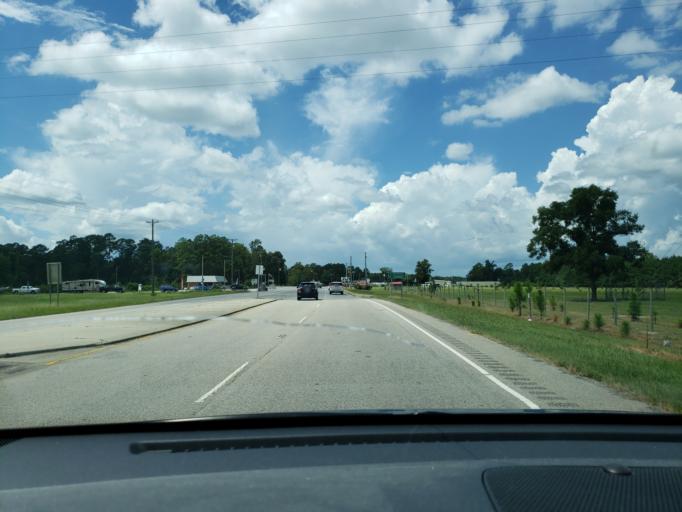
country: US
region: North Carolina
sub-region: Bladen County
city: Bladenboro
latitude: 34.7308
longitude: -78.7843
